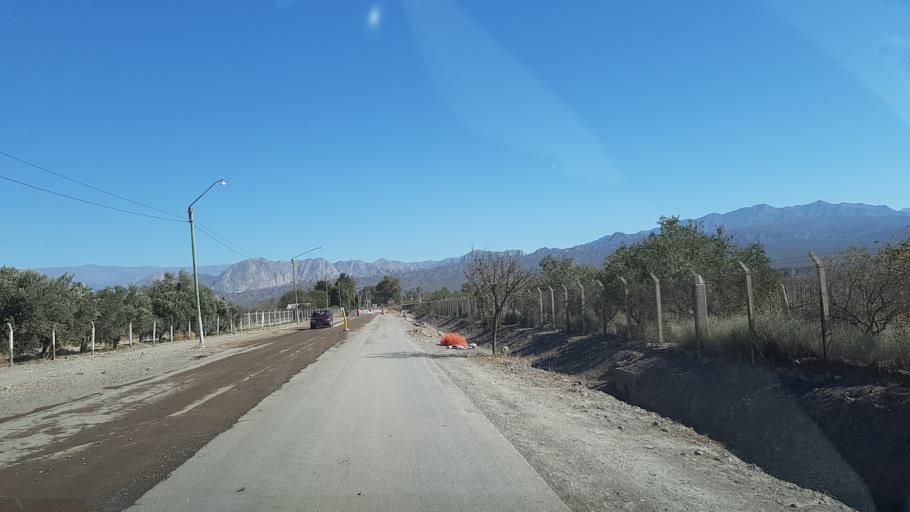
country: AR
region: San Juan
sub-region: Departamento de Zonda
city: Zonda
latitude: -31.4692
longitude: -68.7283
